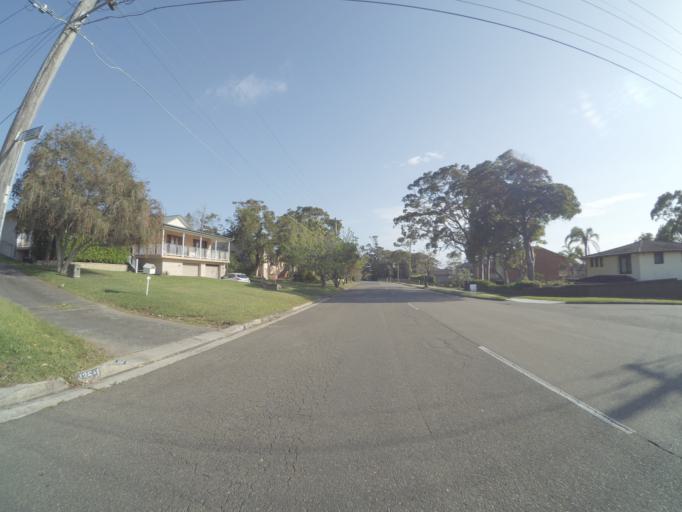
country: AU
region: New South Wales
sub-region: Sutherland Shire
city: Dolans Bay
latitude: -34.0702
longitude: 151.1379
